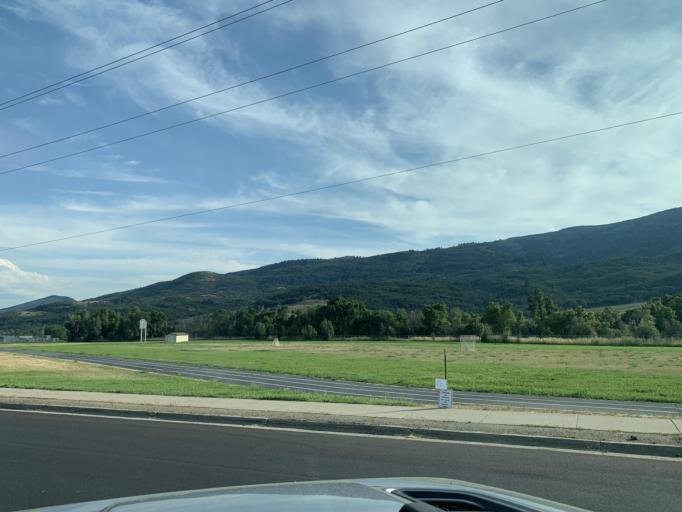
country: US
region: Utah
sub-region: Weber County
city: Wolf Creek
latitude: 41.3109
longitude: -111.8344
